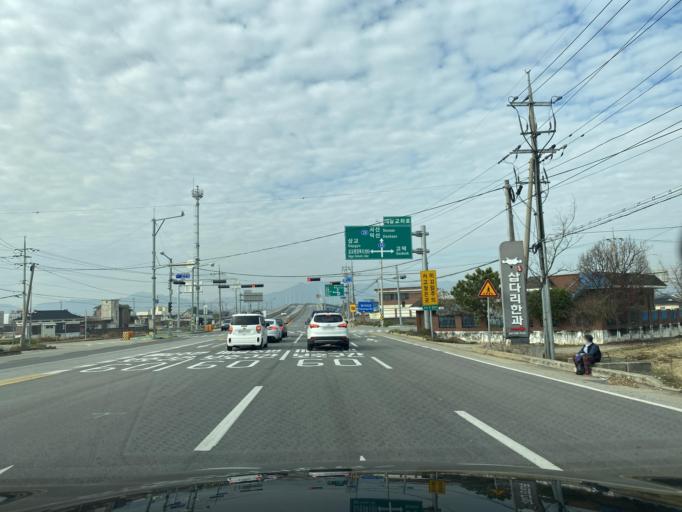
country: KR
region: Chungcheongnam-do
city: Yesan
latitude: 36.6906
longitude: 126.7437
